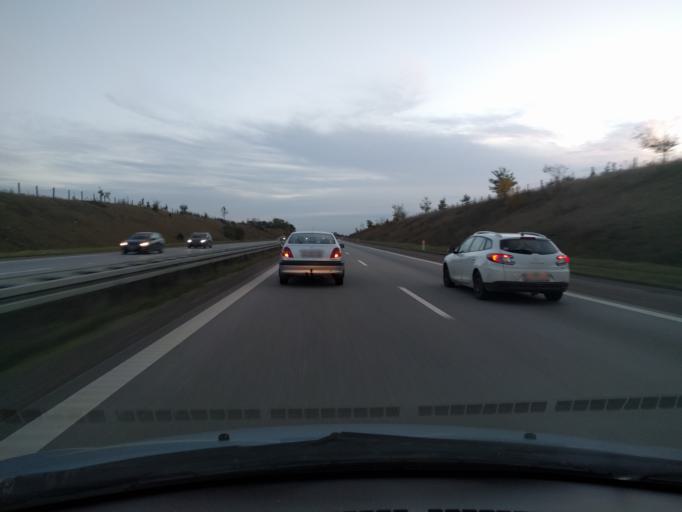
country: DK
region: South Denmark
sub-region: Odense Kommune
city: Hojby
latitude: 55.3367
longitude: 10.4520
